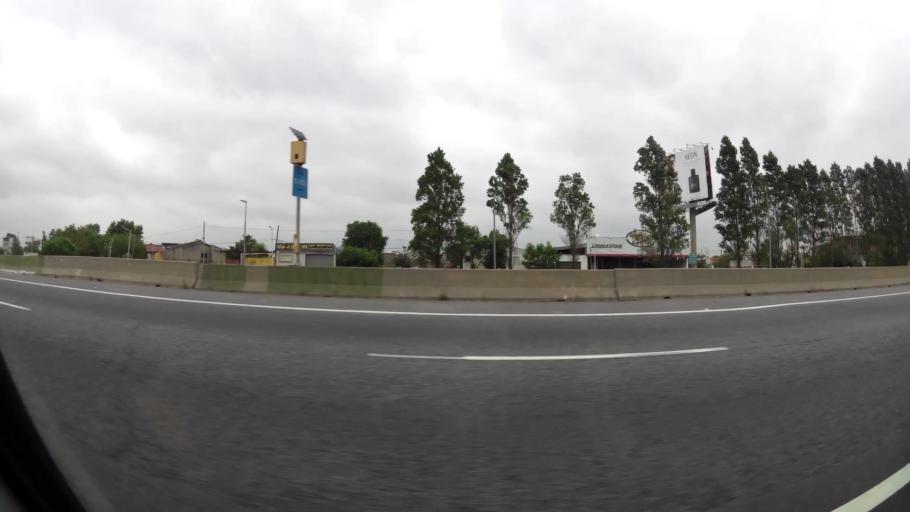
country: AR
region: Buenos Aires
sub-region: Partido de Avellaneda
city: Avellaneda
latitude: -34.6684
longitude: -58.3411
